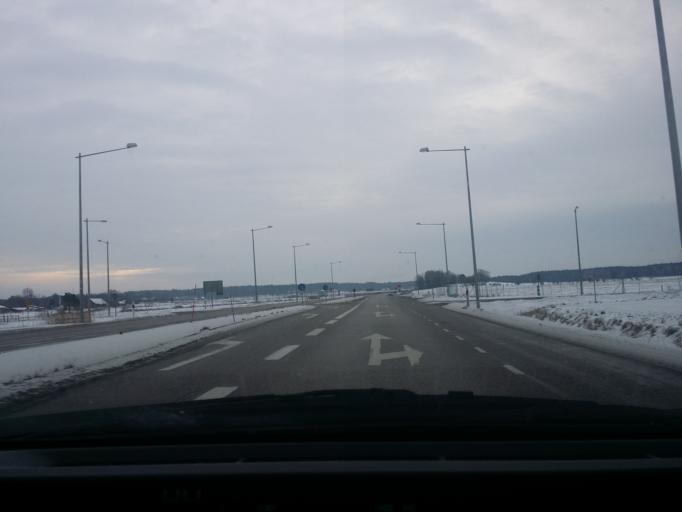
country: SE
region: Vaestra Goetaland
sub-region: Mariestads Kommun
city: Mariestad
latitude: 58.6684
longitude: 13.8195
